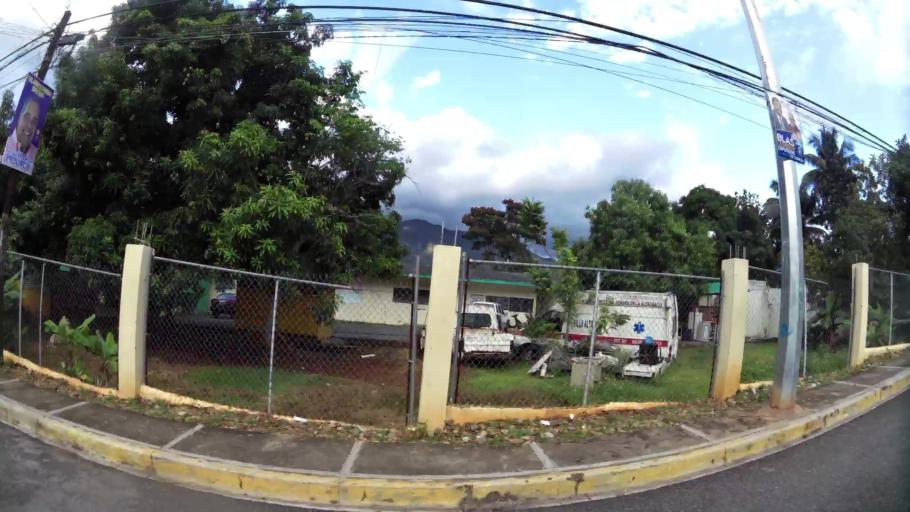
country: DO
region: San Cristobal
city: Villa Altagracia
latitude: 18.6689
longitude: -70.1701
